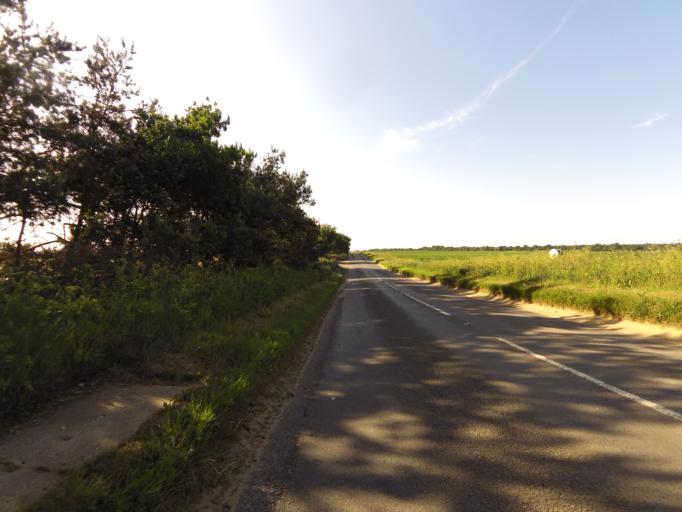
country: GB
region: England
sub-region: Suffolk
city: Woodbridge
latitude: 52.0811
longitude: 1.3611
